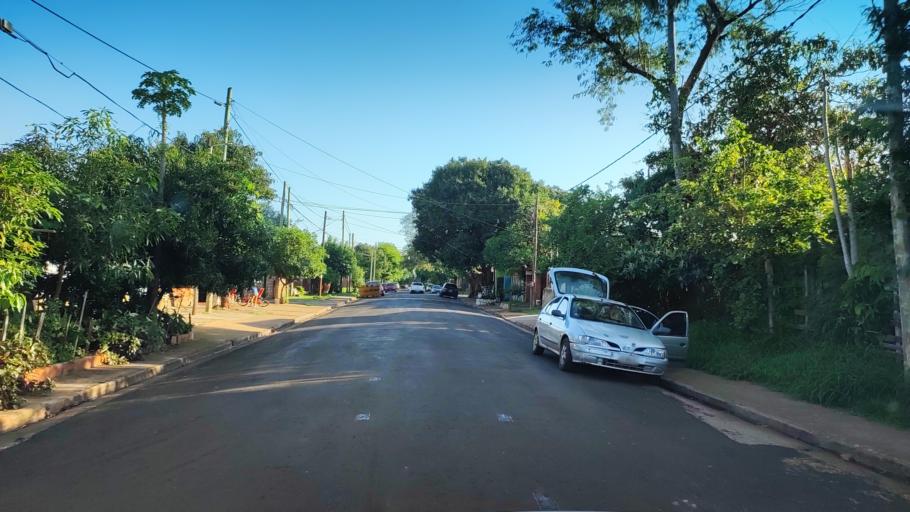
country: AR
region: Misiones
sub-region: Departamento de Capital
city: Posadas
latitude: -27.3813
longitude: -55.9355
